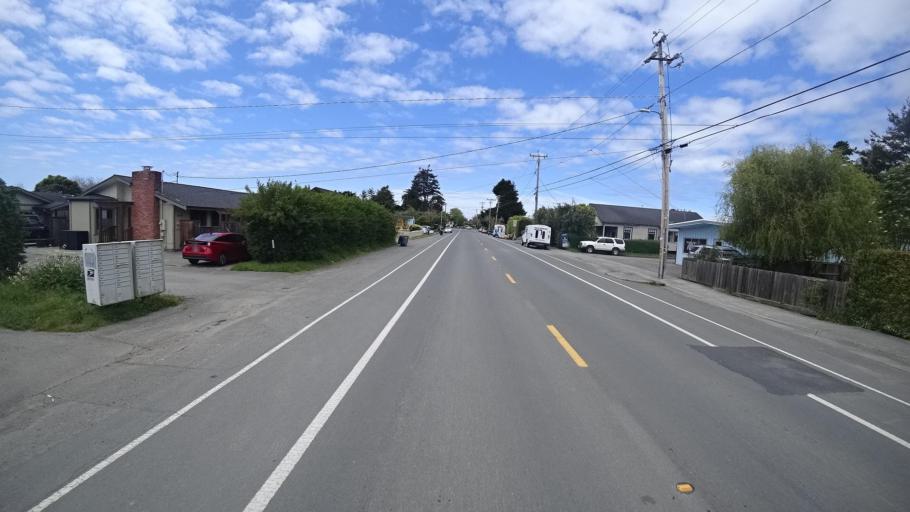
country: US
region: California
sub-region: Humboldt County
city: Arcata
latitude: 40.8896
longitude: -124.0851
